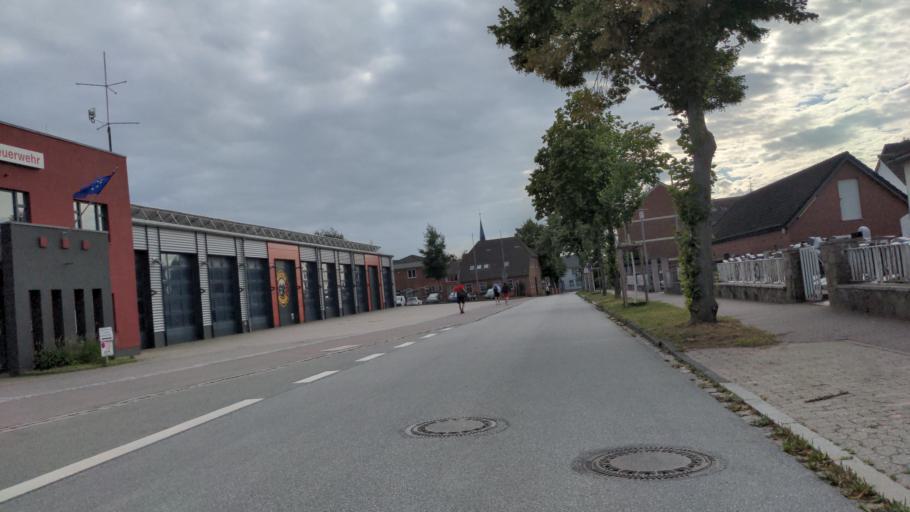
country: DE
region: Schleswig-Holstein
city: Neustadt in Holstein
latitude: 54.1080
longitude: 10.8214
